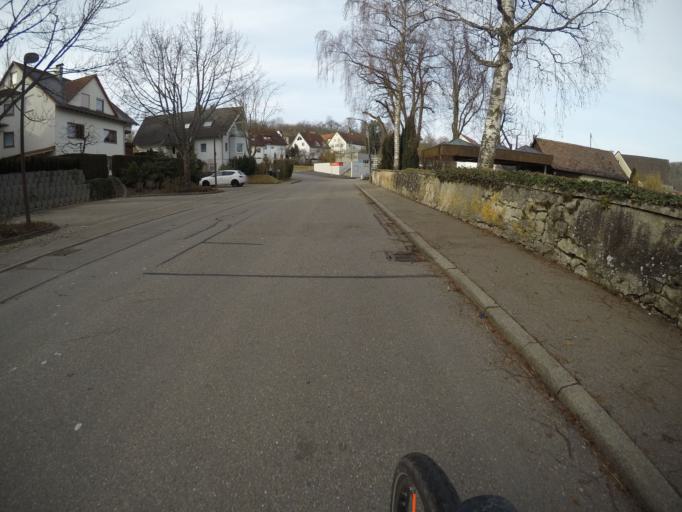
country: DE
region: Baden-Wuerttemberg
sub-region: Regierungsbezirk Stuttgart
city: Aidlingen
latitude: 48.7150
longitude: 8.8866
